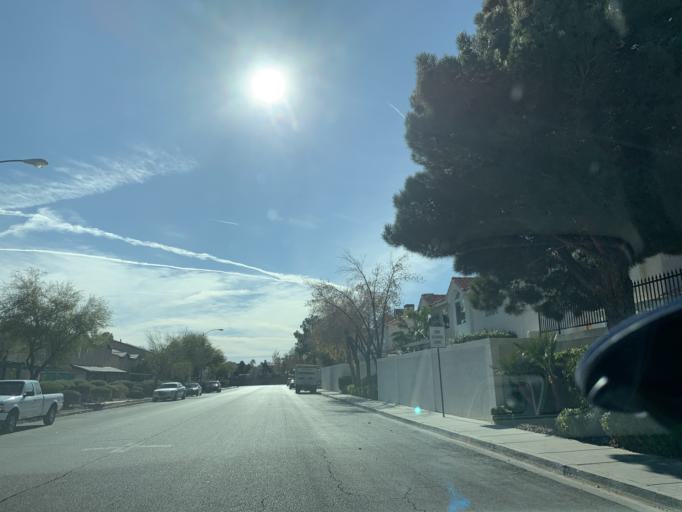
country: US
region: Nevada
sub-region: Clark County
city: Spring Valley
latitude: 36.0944
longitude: -115.2209
